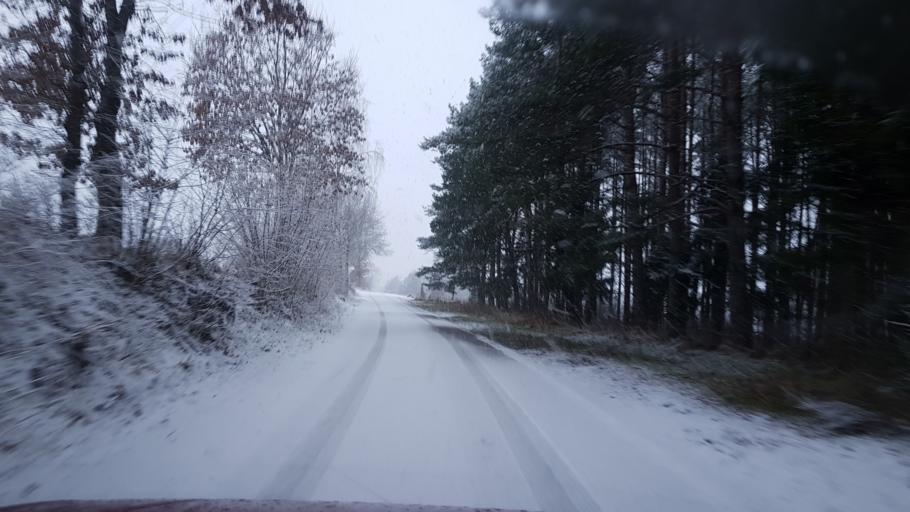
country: PL
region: West Pomeranian Voivodeship
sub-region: Powiat koszalinski
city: Polanow
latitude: 54.2367
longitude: 16.6252
